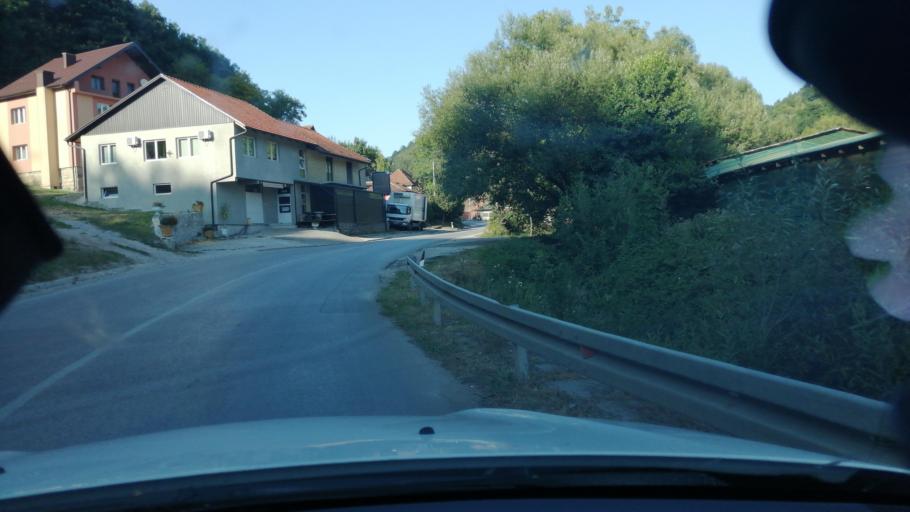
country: RS
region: Central Serbia
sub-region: Moravicki Okrug
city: Ivanjica
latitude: 43.6045
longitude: 20.2322
